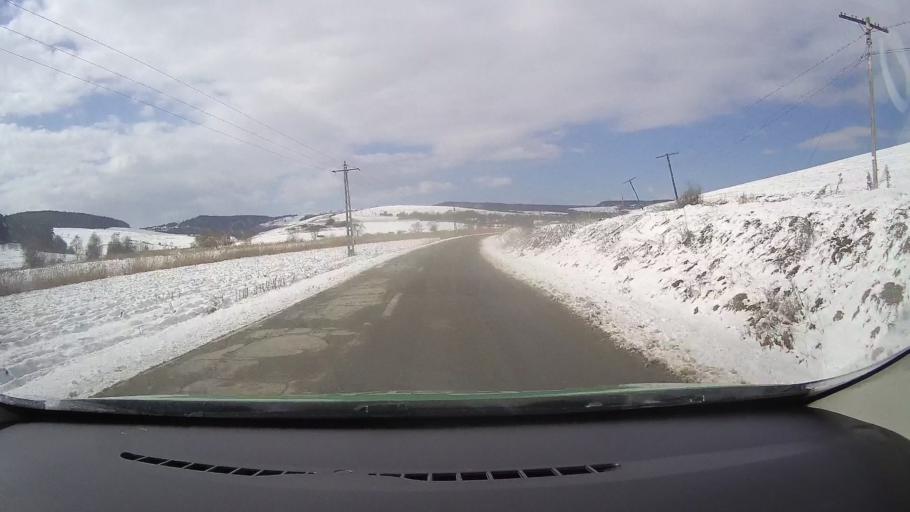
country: RO
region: Sibiu
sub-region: Comuna Altina
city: Altina
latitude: 45.9786
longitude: 24.4642
